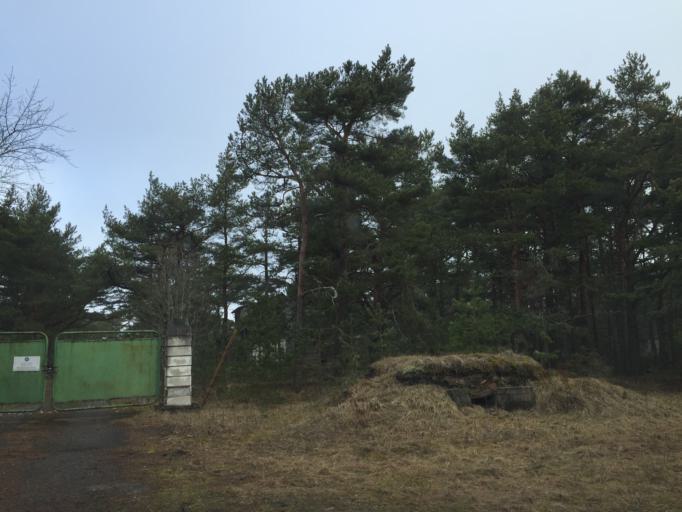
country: EE
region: Saare
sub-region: Kuressaare linn
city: Kuressaare
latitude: 58.1844
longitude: 22.2564
